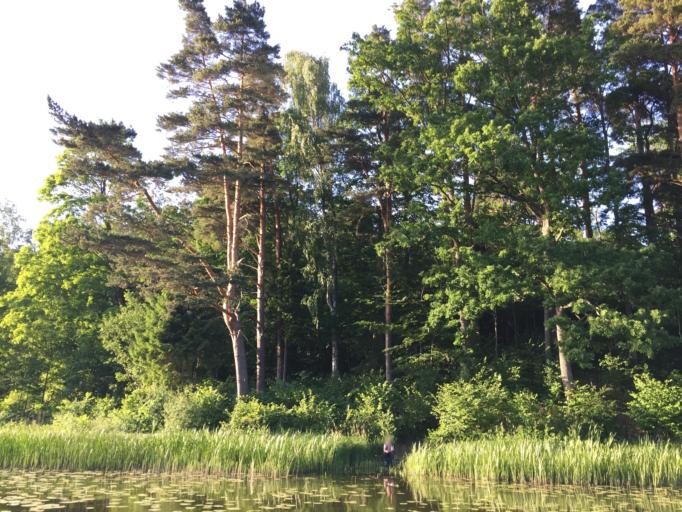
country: LV
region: Aizpute
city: Aizpute
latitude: 56.7268
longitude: 21.7383
